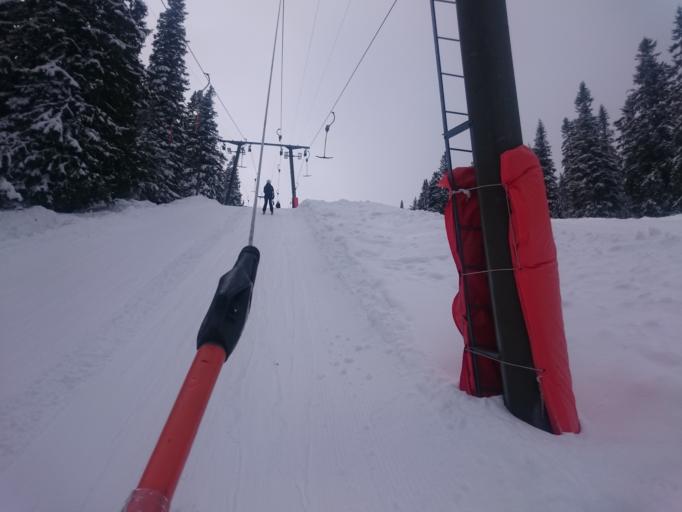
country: SE
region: Dalarna
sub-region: Malung-Saelens kommun
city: Malung
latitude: 61.1627
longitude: 13.1682
